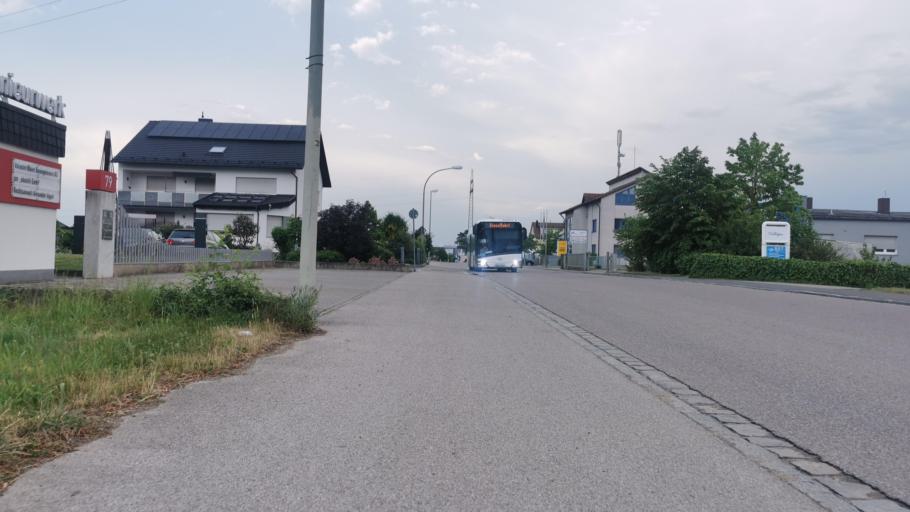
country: DE
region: Bavaria
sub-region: Regierungsbezirk Mittelfranken
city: Hochstadt an der Aisch
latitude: 49.7034
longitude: 10.8208
